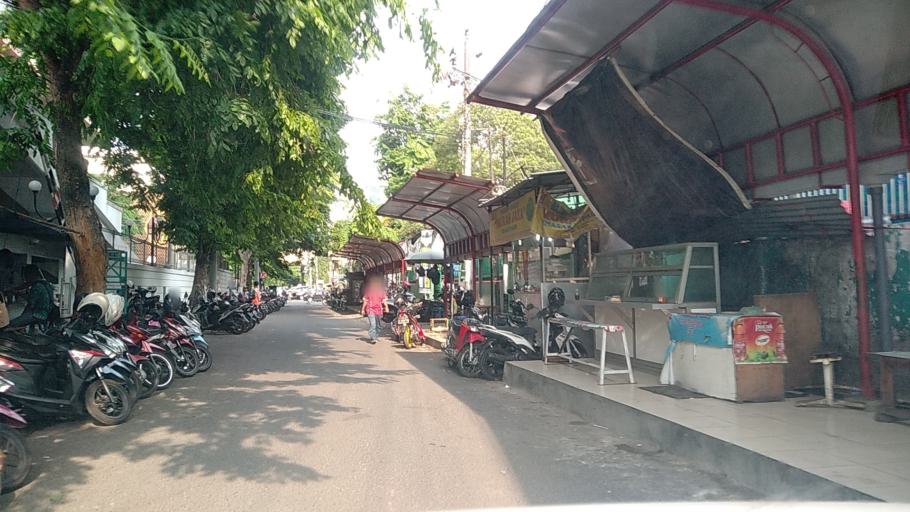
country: ID
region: Central Java
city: Semarang
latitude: -6.9884
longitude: 110.4220
